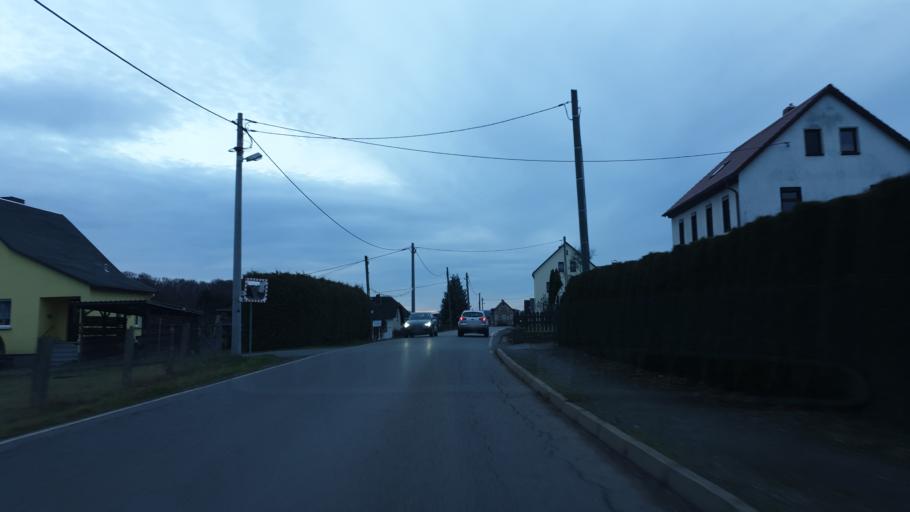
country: DE
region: Saxony
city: Hartenstein
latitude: 50.6845
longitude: 12.6695
